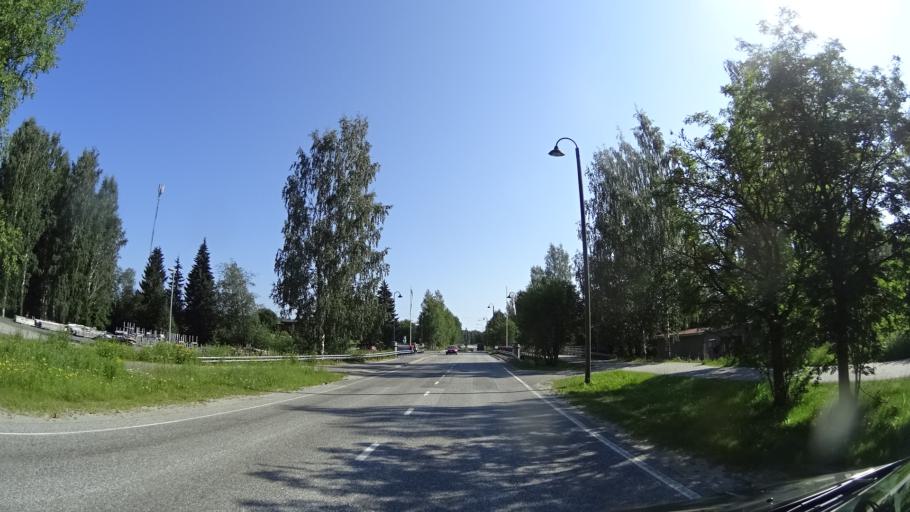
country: FI
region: North Karelia
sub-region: Joensuu
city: Juuka
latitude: 63.2448
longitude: 29.2594
